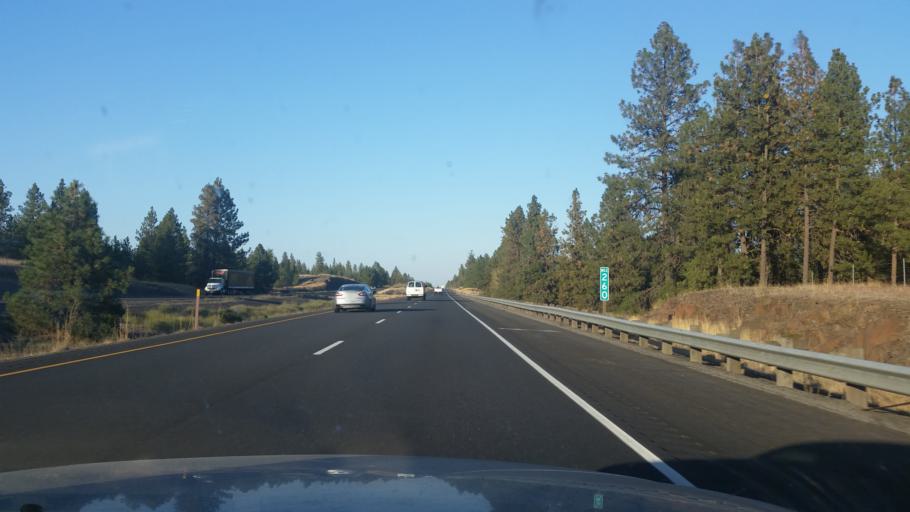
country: US
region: Washington
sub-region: Spokane County
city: Medical Lake
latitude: 47.4595
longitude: -117.7566
